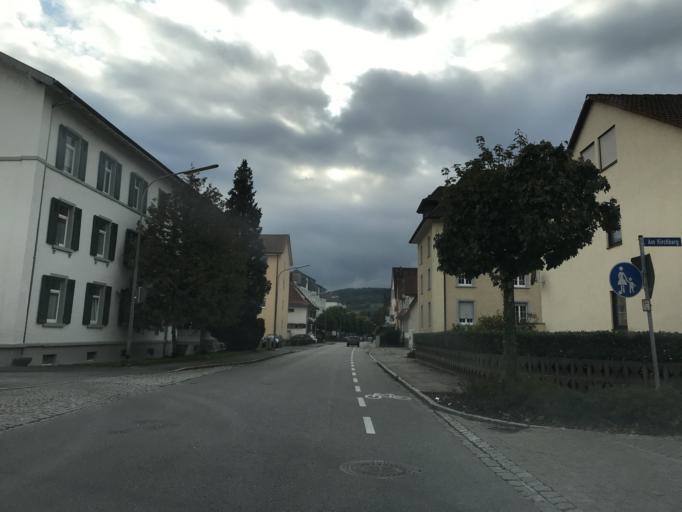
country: DE
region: Baden-Wuerttemberg
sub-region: Freiburg Region
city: Loerrach
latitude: 47.6302
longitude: 7.6612
